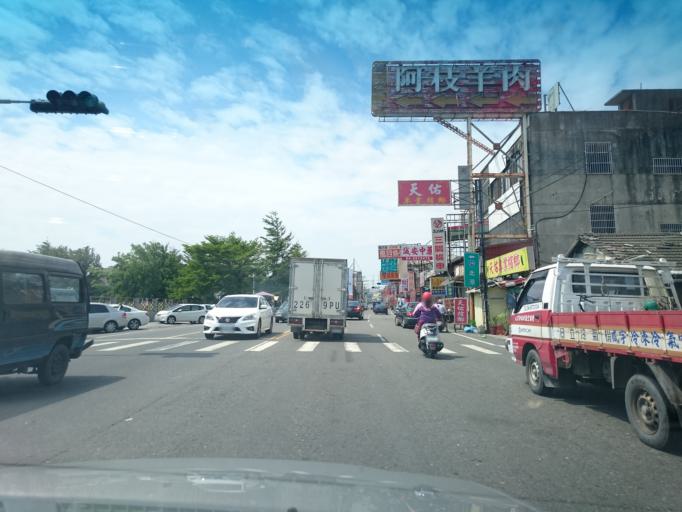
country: TW
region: Taiwan
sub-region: Changhua
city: Chang-hua
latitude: 23.9572
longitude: 120.4842
